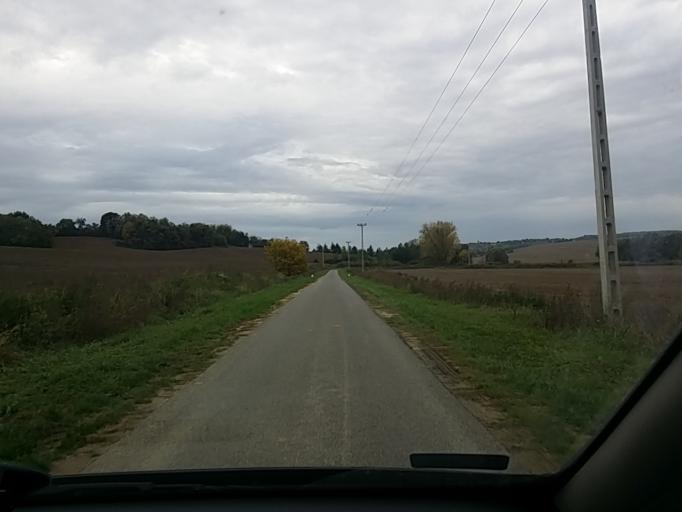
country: HU
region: Somogy
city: Kaposmero
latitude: 46.2840
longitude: 17.7401
